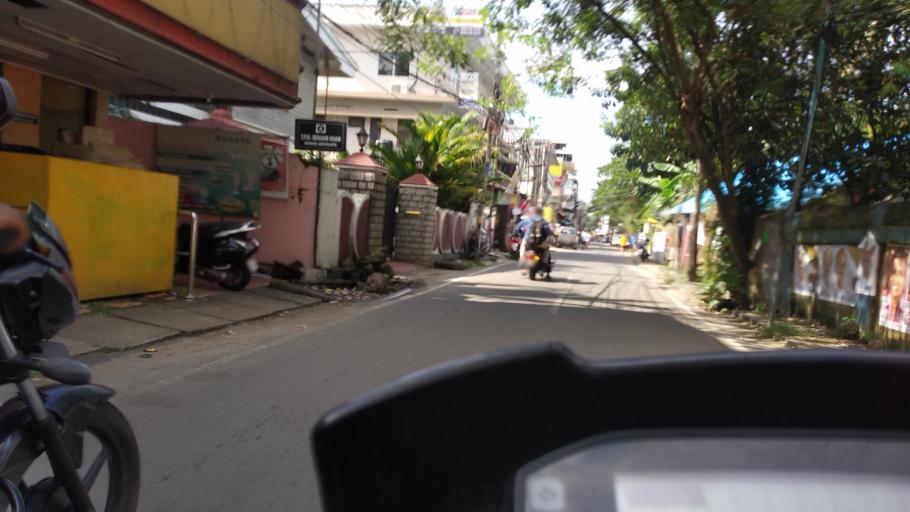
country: IN
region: Kerala
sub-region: Ernakulam
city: Cochin
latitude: 9.9927
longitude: 76.2873
